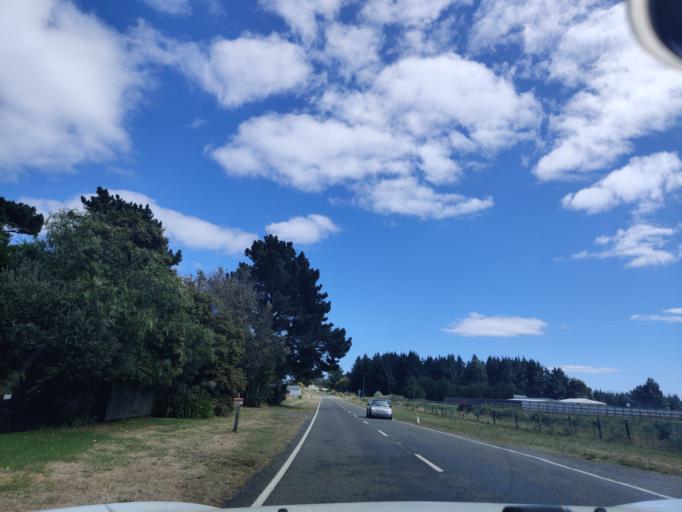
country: NZ
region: Manawatu-Wanganui
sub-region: Horowhenua District
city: Foxton
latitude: -40.3721
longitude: 175.2467
